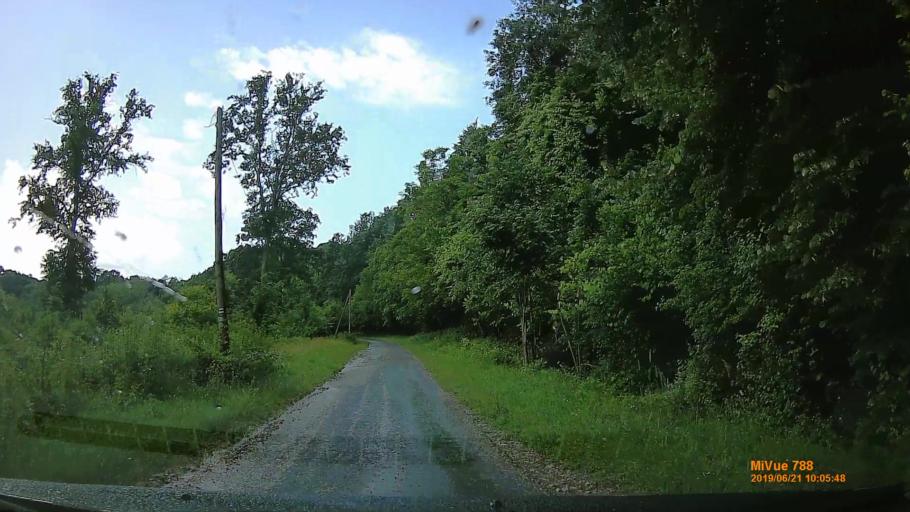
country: HU
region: Baranya
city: Buekkoesd
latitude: 46.1967
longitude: 17.9599
